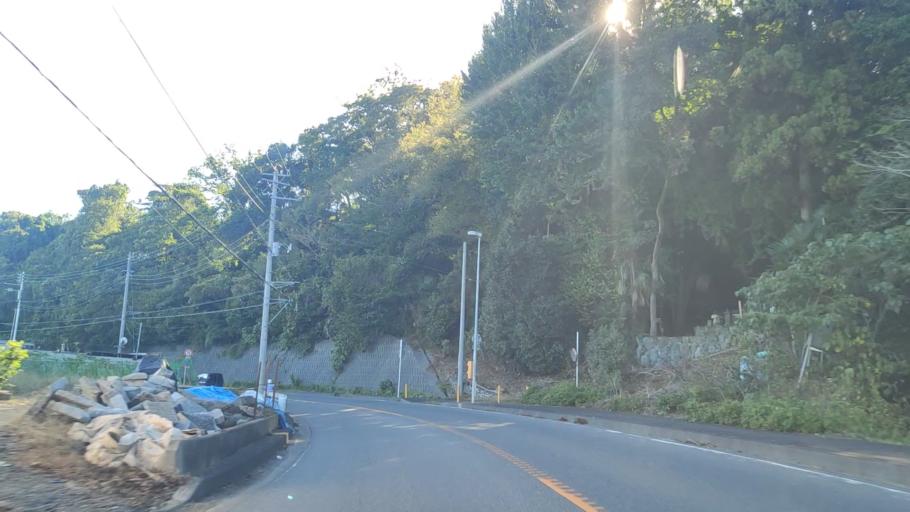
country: JP
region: Kanagawa
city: Zama
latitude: 35.5492
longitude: 139.3199
